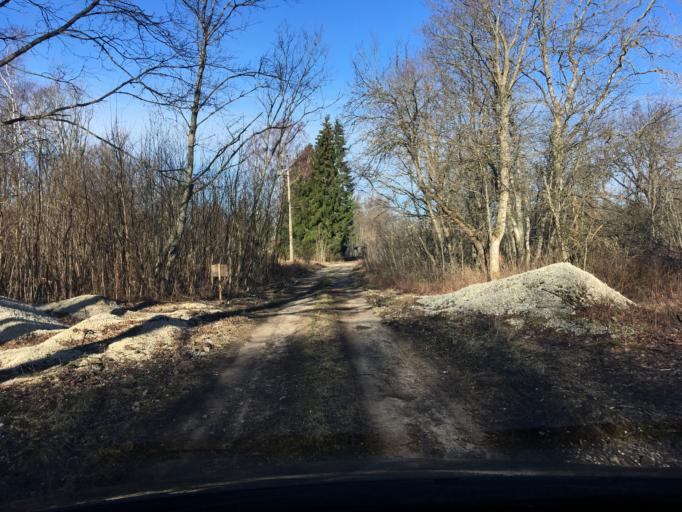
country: EE
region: Laeaene
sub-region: Lihula vald
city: Lihula
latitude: 58.5835
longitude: 23.7195
